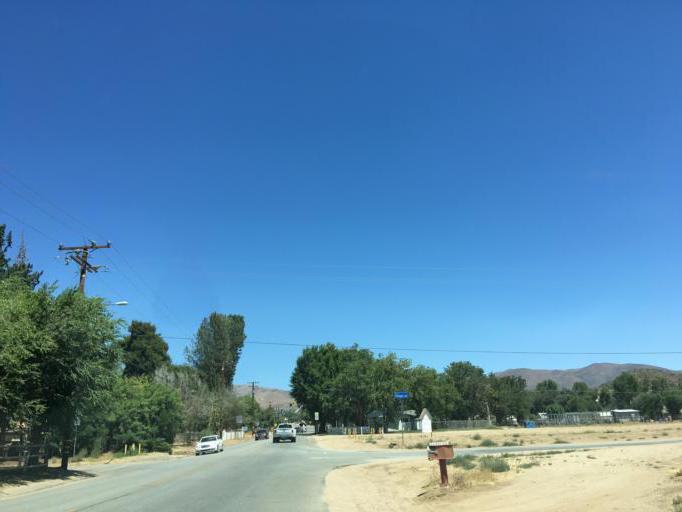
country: US
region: California
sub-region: Los Angeles County
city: Acton
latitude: 34.4695
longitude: -118.1972
